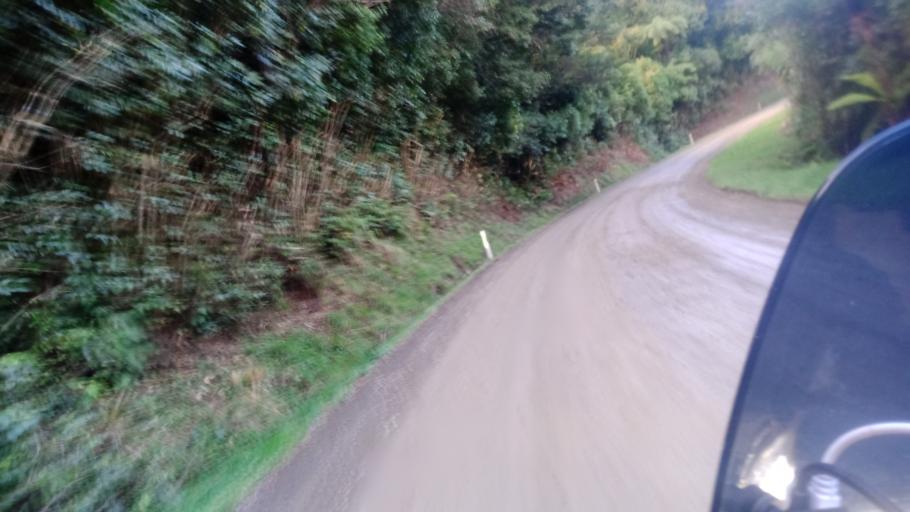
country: NZ
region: Hawke's Bay
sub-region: Wairoa District
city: Wairoa
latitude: -38.7441
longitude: 177.1174
